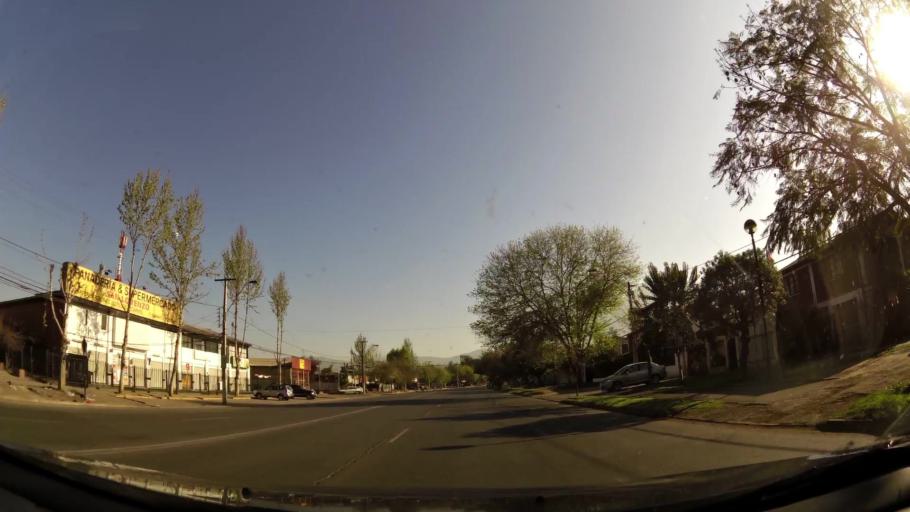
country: CL
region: Santiago Metropolitan
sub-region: Provincia de Santiago
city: Santiago
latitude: -33.3794
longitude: -70.6576
